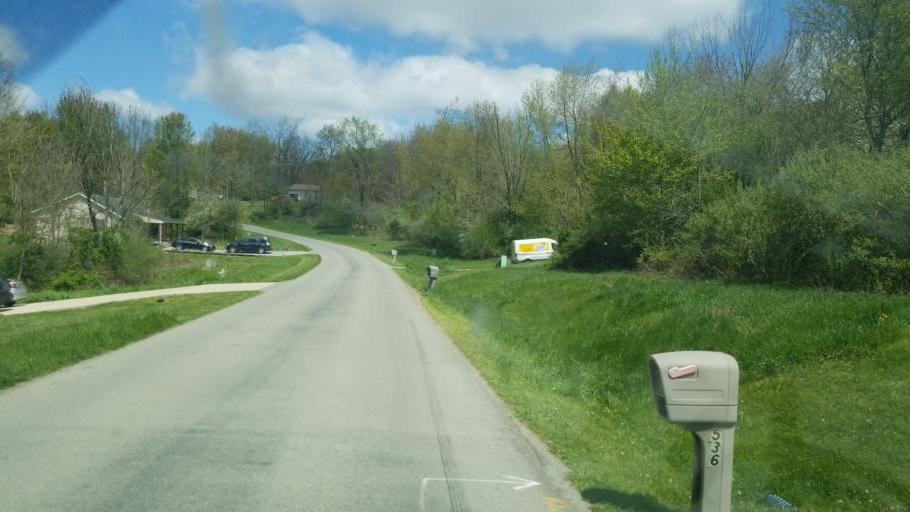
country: US
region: Ohio
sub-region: Knox County
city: Gambier
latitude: 40.4425
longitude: -82.3646
